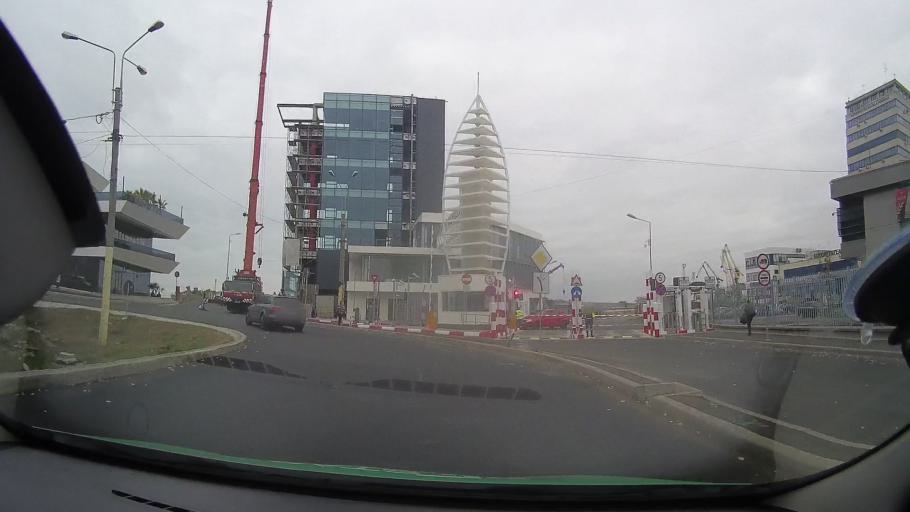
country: RO
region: Constanta
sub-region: Municipiul Constanta
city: Constanta
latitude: 44.1704
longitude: 28.6596
